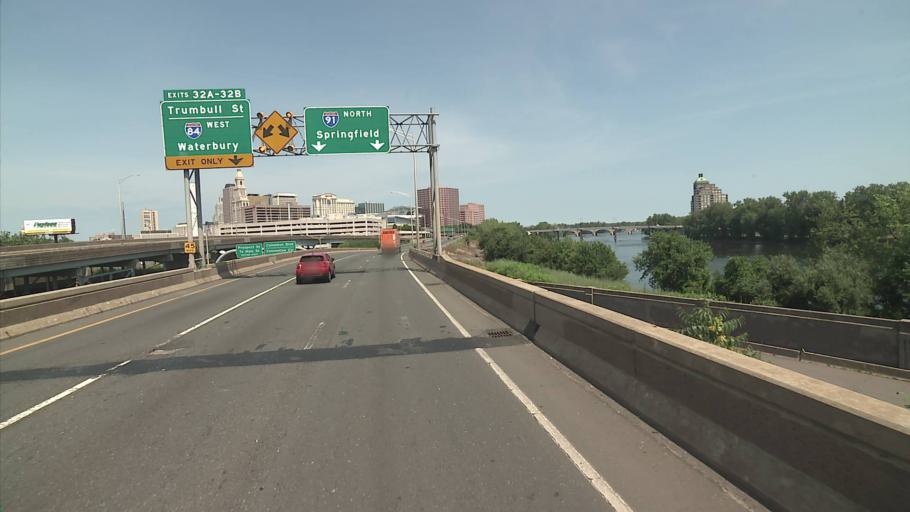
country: US
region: Connecticut
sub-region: Hartford County
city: Hartford
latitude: 41.7593
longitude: -72.6645
